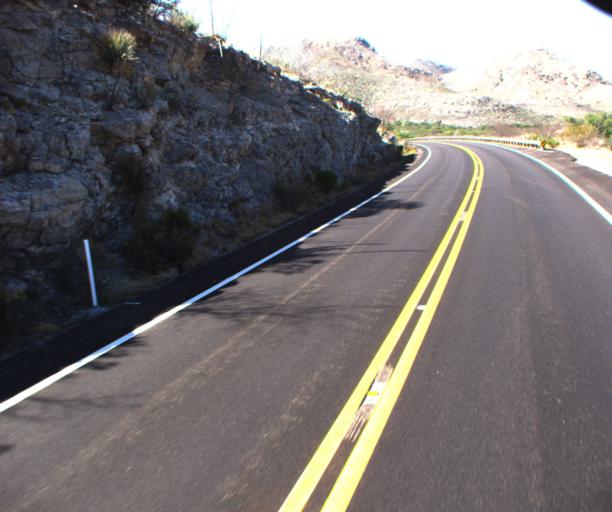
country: US
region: Arizona
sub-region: Cochise County
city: Bisbee
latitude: 31.5207
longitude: -110.0166
